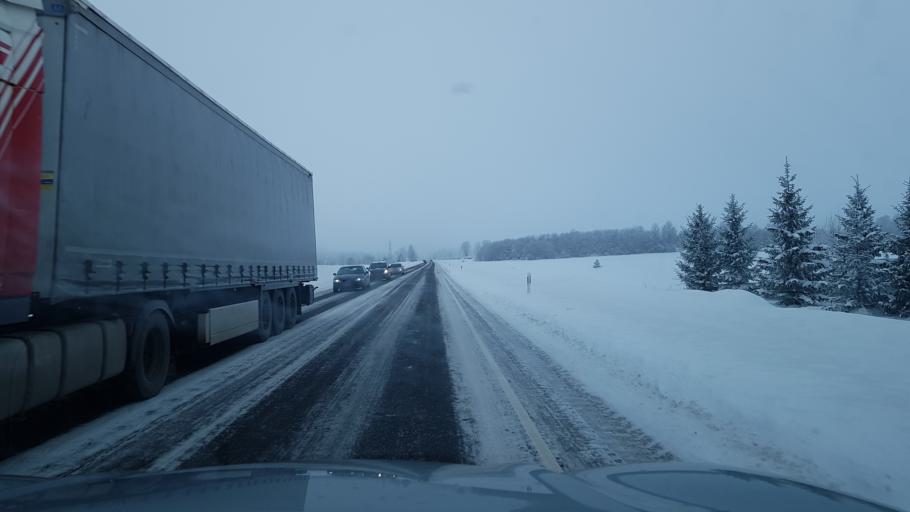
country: EE
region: Ida-Virumaa
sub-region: Johvi vald
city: Johvi
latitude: 59.2460
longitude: 27.3674
